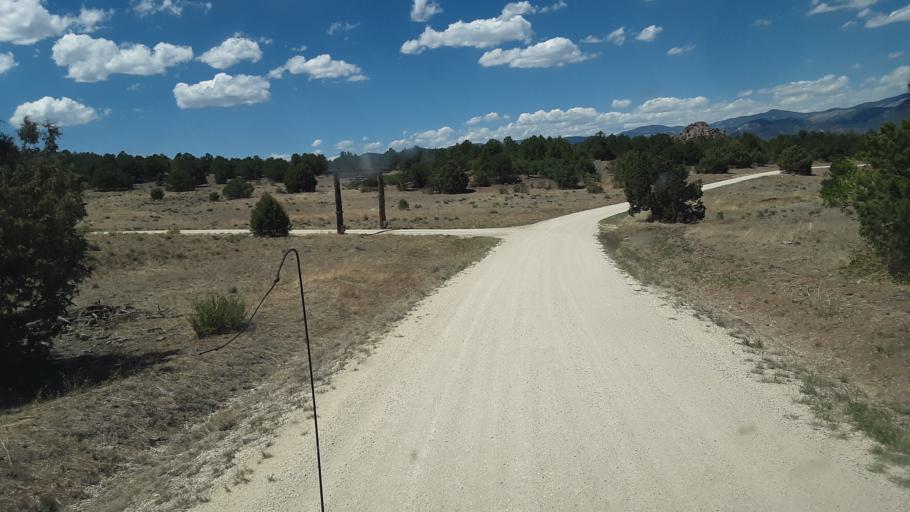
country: US
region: Colorado
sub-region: Custer County
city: Westcliffe
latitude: 38.3221
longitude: -105.6253
